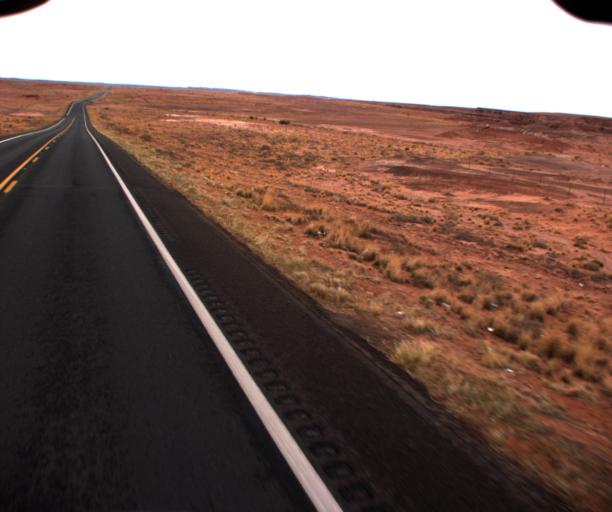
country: US
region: Arizona
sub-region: Coconino County
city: Tuba City
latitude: 36.1026
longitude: -111.2896
